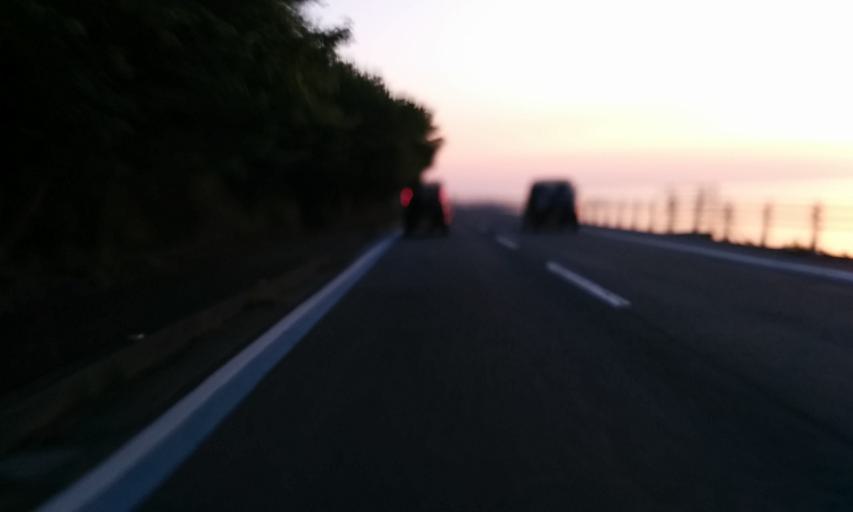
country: JP
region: Ehime
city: Ozu
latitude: 33.6396
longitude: 132.5392
